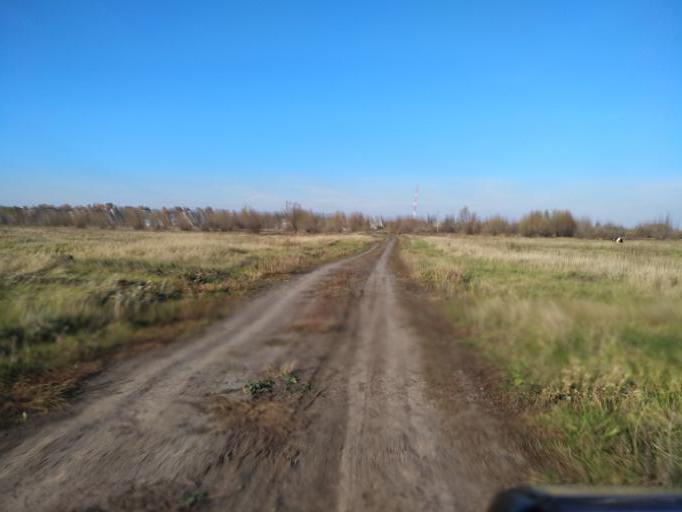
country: RU
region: Lipetsk
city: Dobrinka
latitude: 52.0263
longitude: 40.5554
